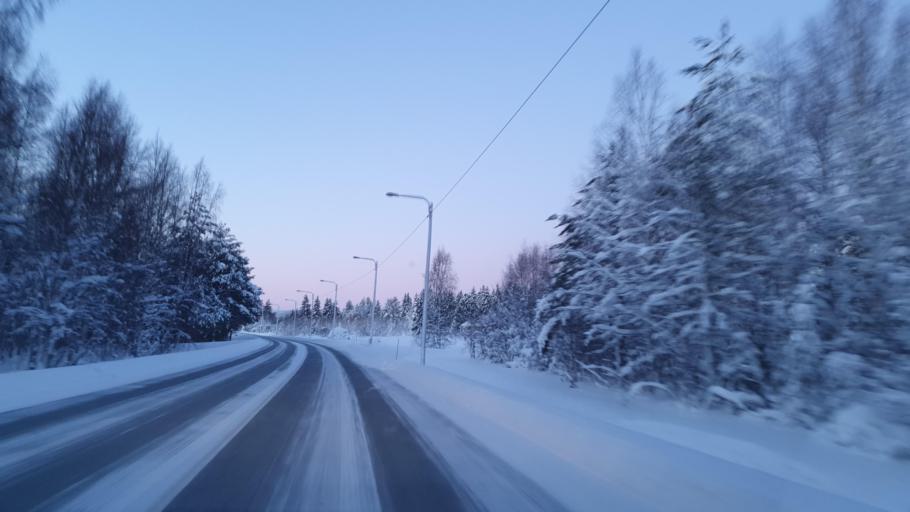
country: FI
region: Lapland
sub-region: Torniolaakso
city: Ylitornio
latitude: 66.2791
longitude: 23.6969
